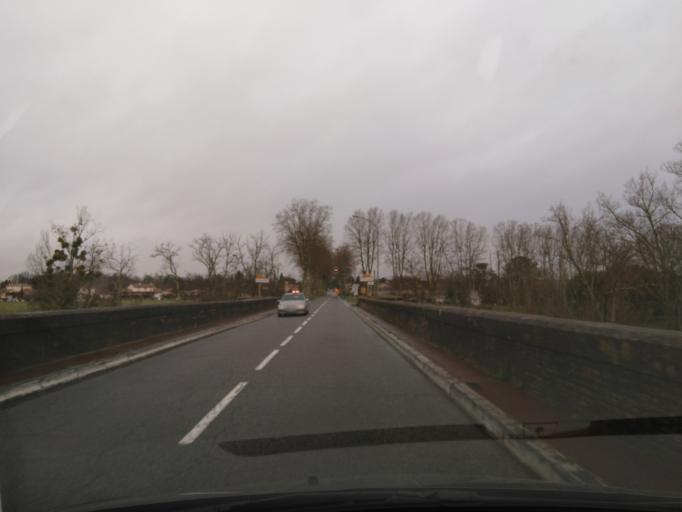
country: FR
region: Midi-Pyrenees
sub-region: Departement de la Haute-Garonne
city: Carbonne
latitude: 43.2898
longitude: 1.2166
